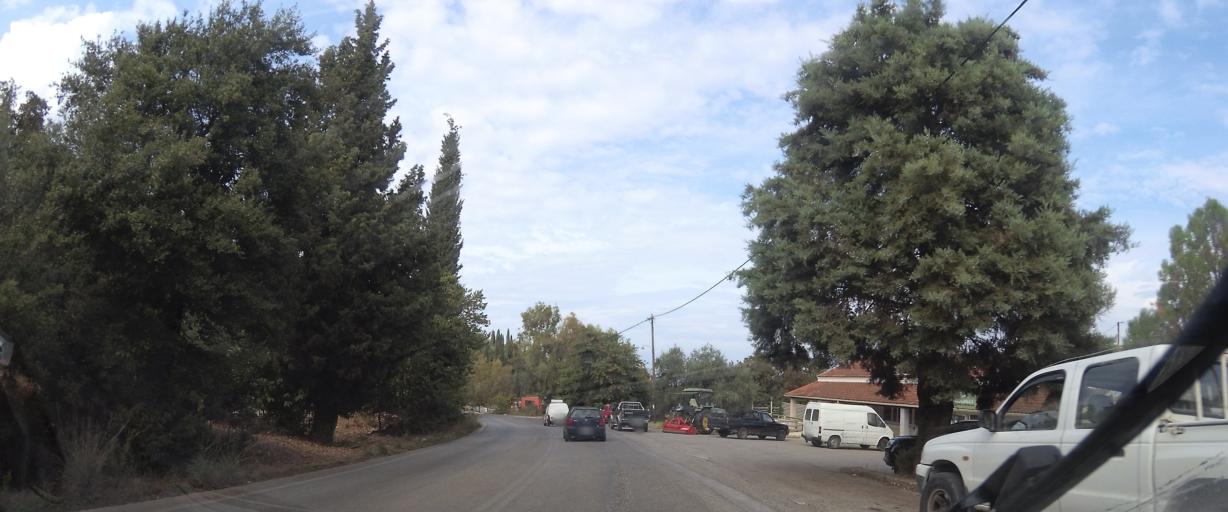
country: GR
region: Ionian Islands
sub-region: Nomos Kerkyras
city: Acharavi
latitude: 39.7630
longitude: 19.9325
